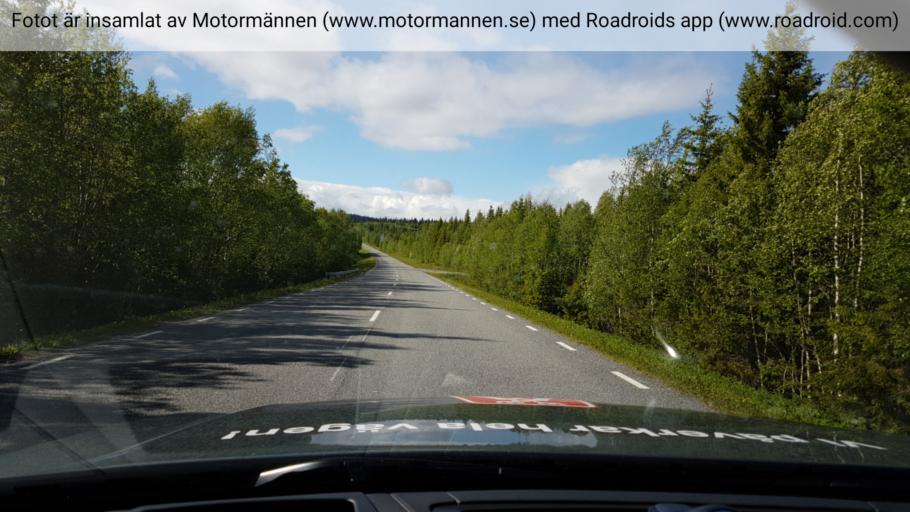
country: SE
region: Jaemtland
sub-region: Are Kommun
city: Are
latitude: 63.6924
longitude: 12.9785
